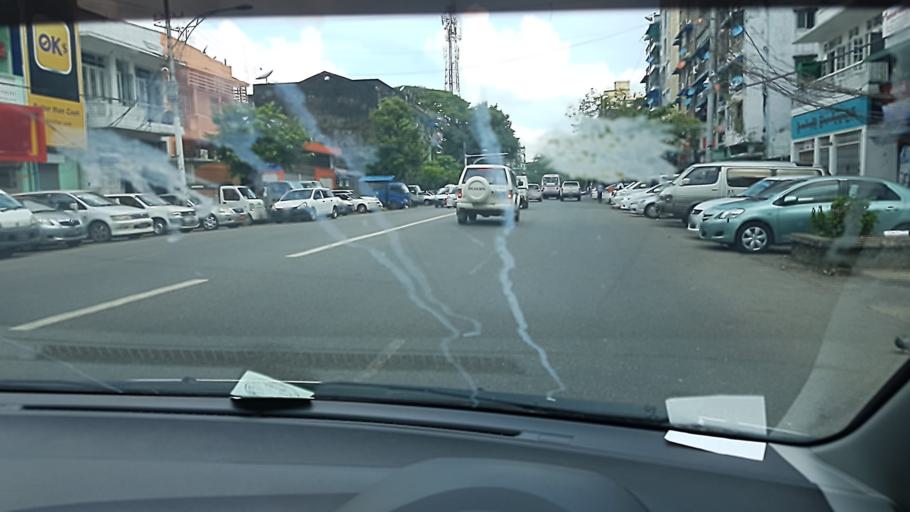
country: MM
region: Yangon
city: Yangon
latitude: 16.7854
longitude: 96.1677
